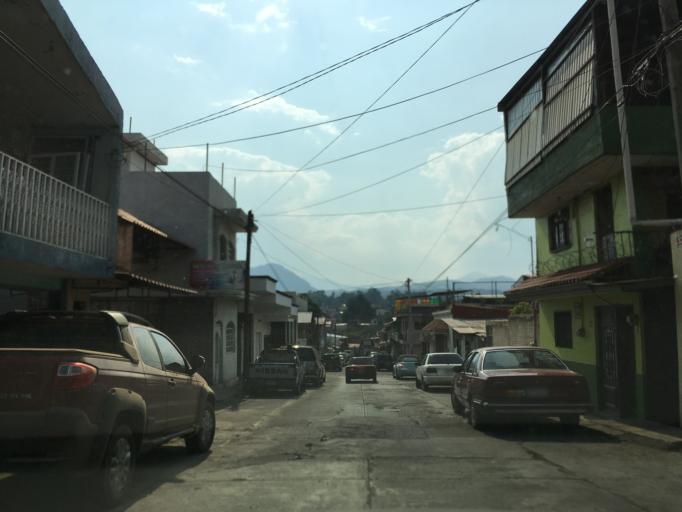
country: MX
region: Michoacan
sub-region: Uruapan
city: Uruapan
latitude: 19.4089
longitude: -102.0593
